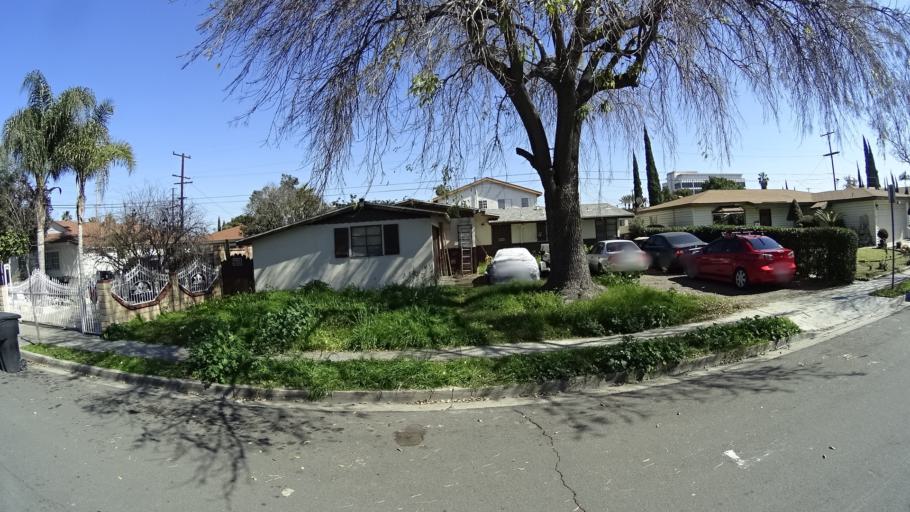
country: US
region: California
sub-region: Orange County
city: Anaheim
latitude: 33.8391
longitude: -117.9441
